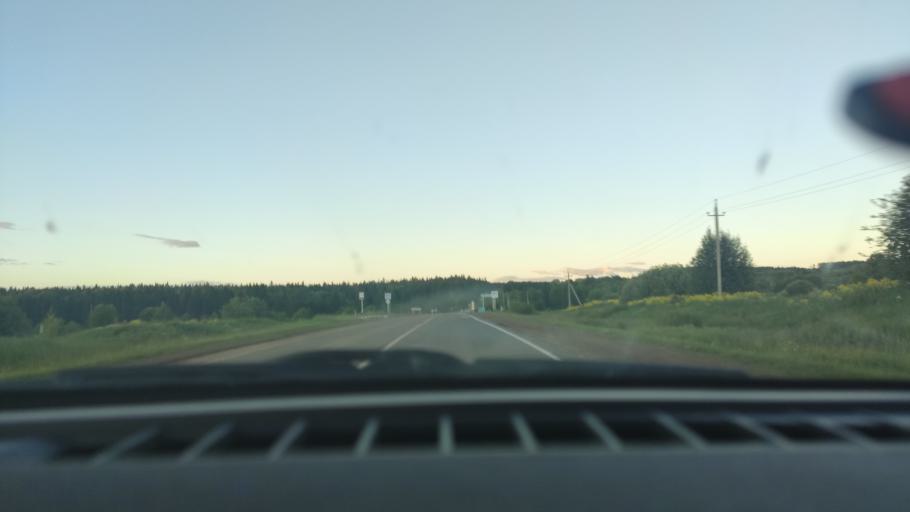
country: RU
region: Perm
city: Chaykovskaya
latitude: 58.5548
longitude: 55.7189
